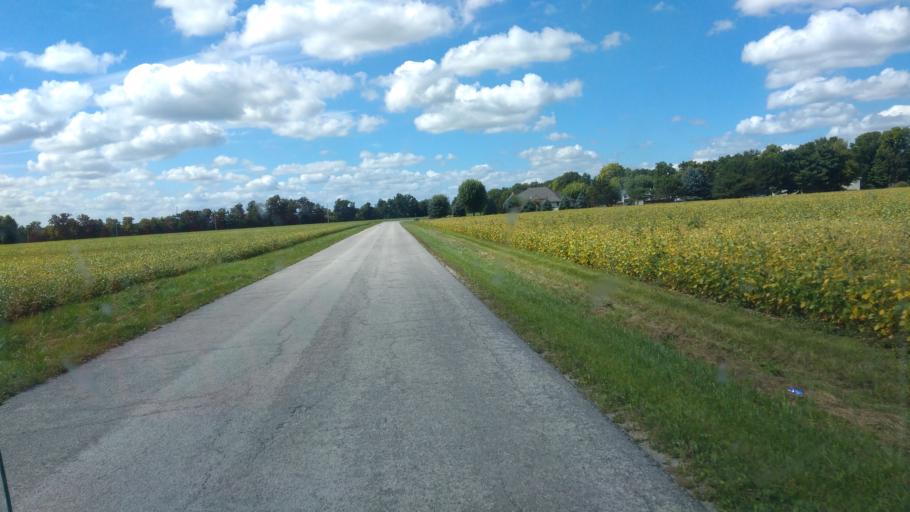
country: US
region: Ohio
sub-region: Huron County
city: Monroeville
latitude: 41.2576
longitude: -82.6767
